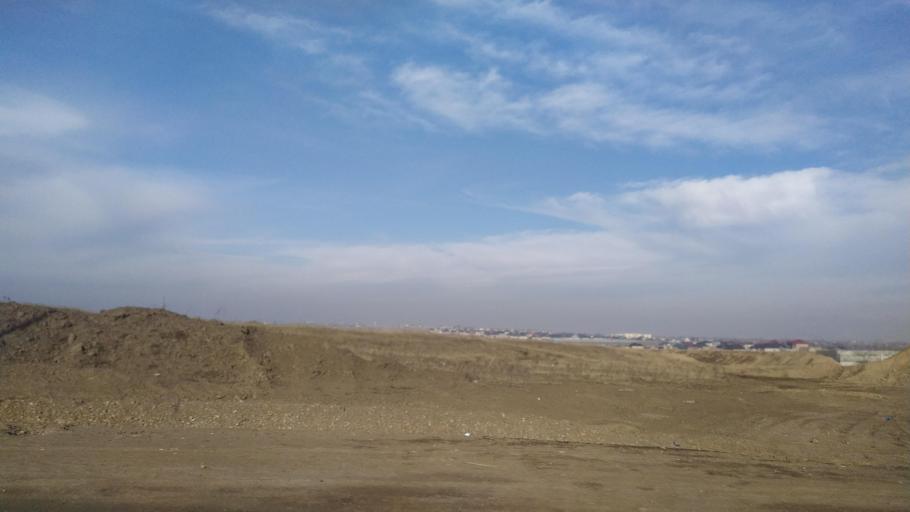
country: KZ
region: Almaty Oblysy
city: Burunday
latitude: 43.2239
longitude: 76.7272
